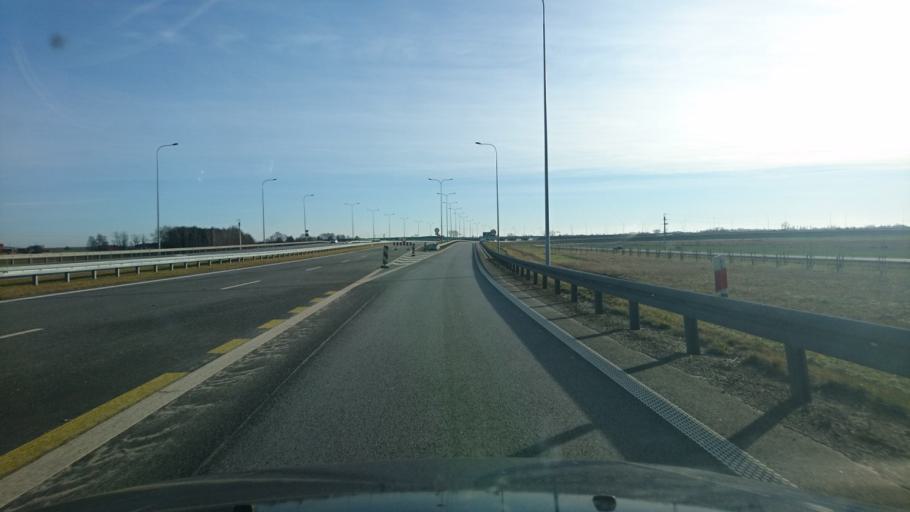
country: PL
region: Greater Poland Voivodeship
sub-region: Powiat kepinski
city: Kepno
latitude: 51.3213
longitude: 18.0025
